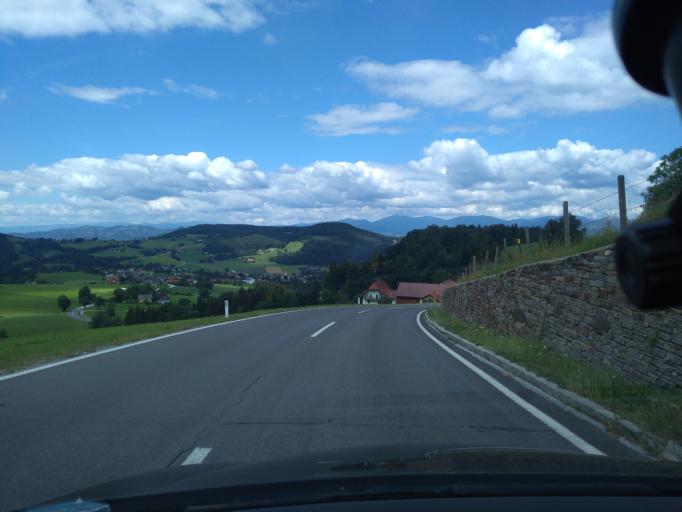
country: AT
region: Styria
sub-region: Politischer Bezirk Graz-Umgebung
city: Semriach
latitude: 47.2207
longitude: 15.4224
